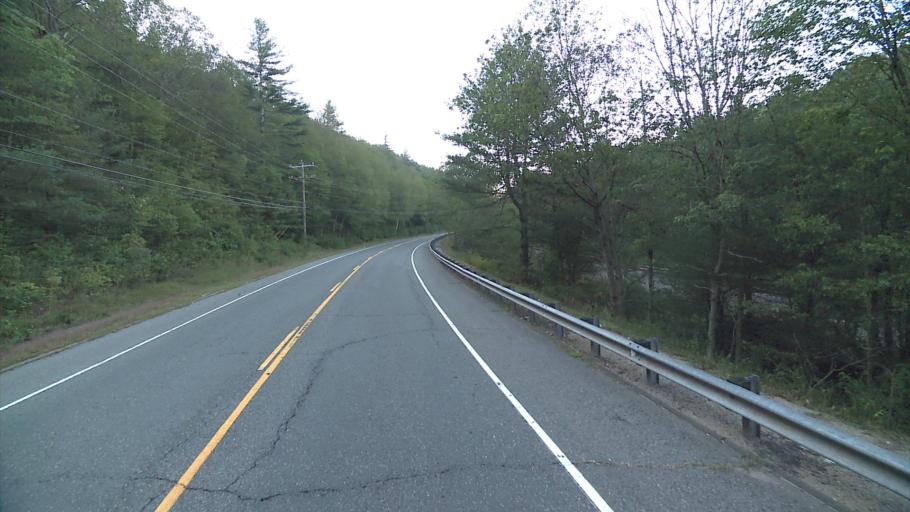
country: US
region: Connecticut
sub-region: Tolland County
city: Stafford Springs
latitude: 41.9184
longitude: -72.2974
